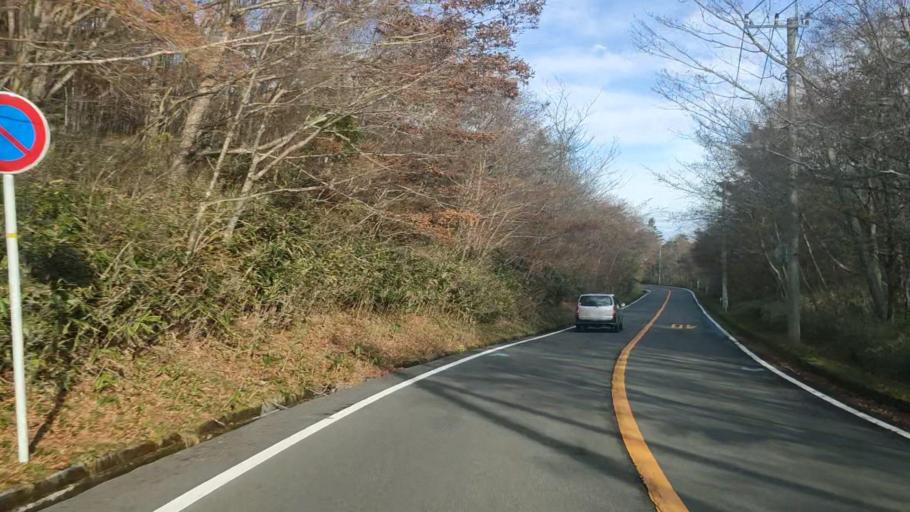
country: JP
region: Shizuoka
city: Gotemba
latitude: 35.3316
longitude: 138.8054
